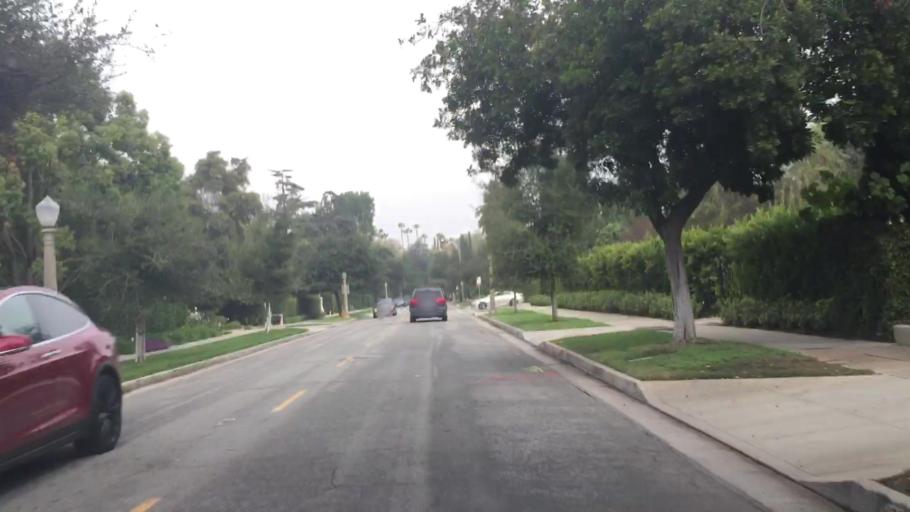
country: US
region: California
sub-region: Los Angeles County
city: San Marino
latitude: 34.1286
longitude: -118.1285
